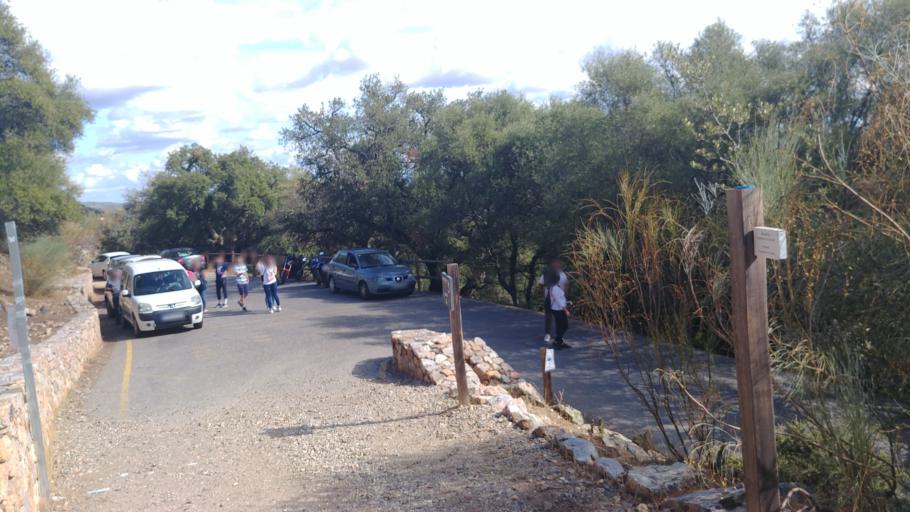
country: ES
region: Extremadura
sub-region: Provincia de Caceres
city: Torrejon el Rubio
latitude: 39.8274
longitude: -6.0498
